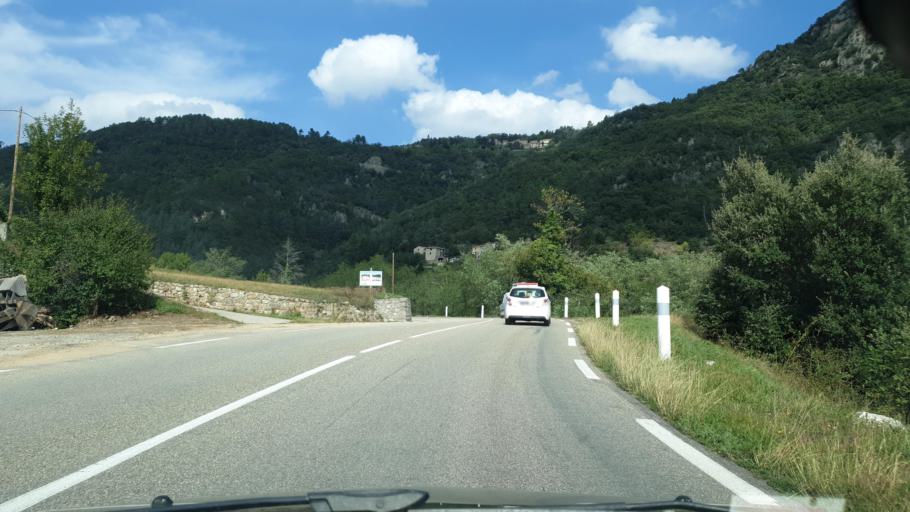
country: FR
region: Rhone-Alpes
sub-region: Departement de l'Ardeche
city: Saint-Sauveur-de-Montagut
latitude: 44.8197
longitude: 4.6165
